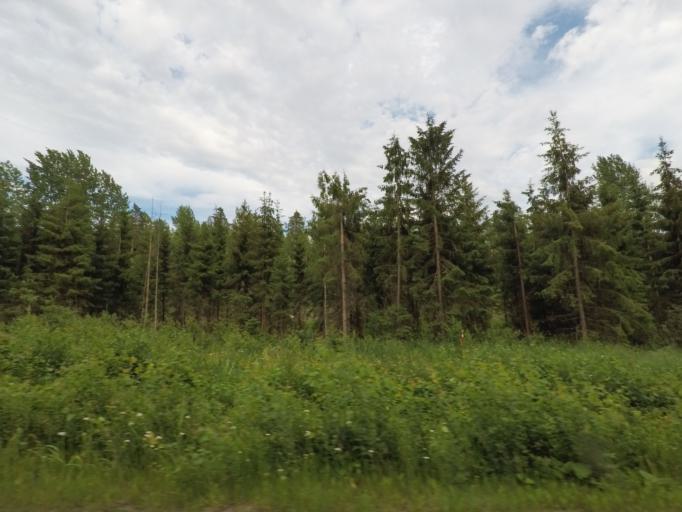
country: FI
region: Paijanne Tavastia
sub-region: Lahti
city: Hollola
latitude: 60.8674
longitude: 25.5015
